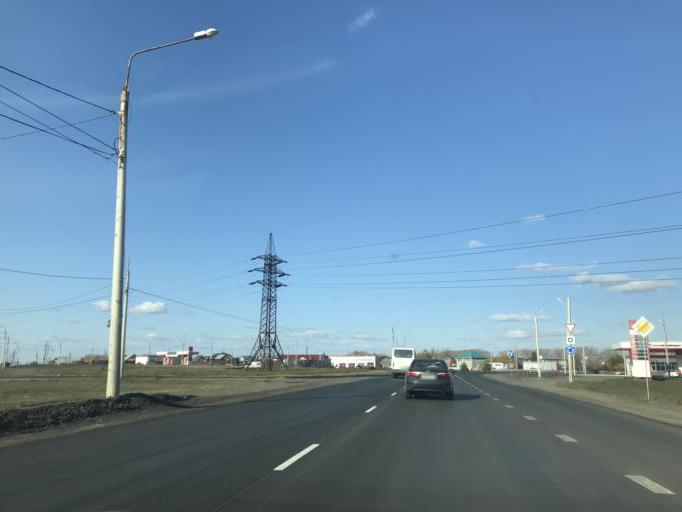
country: RU
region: Chelyabinsk
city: Roshchino
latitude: 55.2291
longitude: 61.2871
